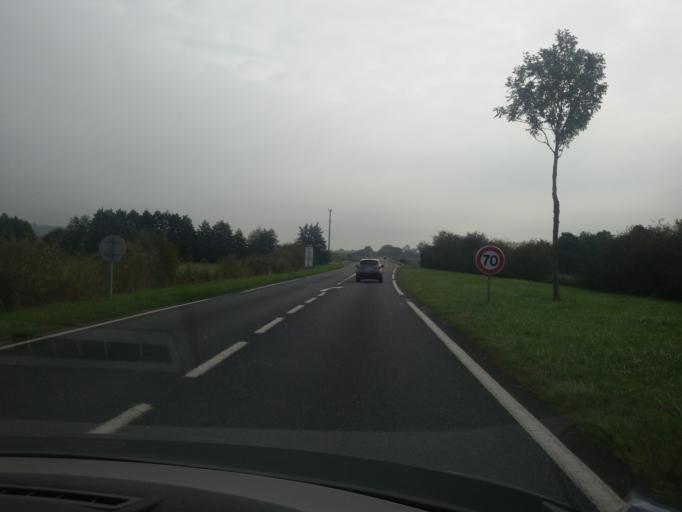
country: FR
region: Lower Normandy
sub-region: Departement du Calvados
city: Dozule
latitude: 49.2330
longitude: -0.0893
